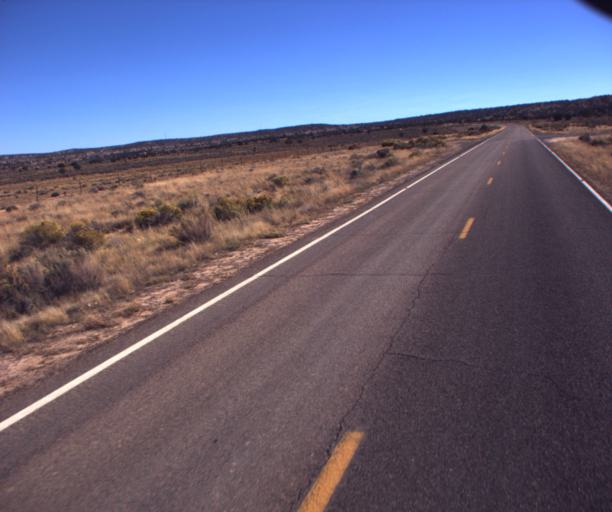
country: US
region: Arizona
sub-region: Navajo County
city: First Mesa
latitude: 35.7523
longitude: -110.1334
